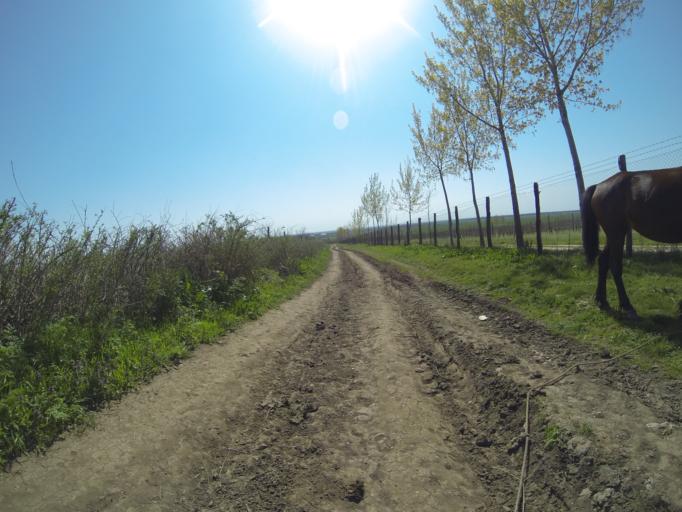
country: RO
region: Dolj
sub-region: Comuna Segarcea
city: Segarcea
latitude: 44.1023
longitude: 23.7259
